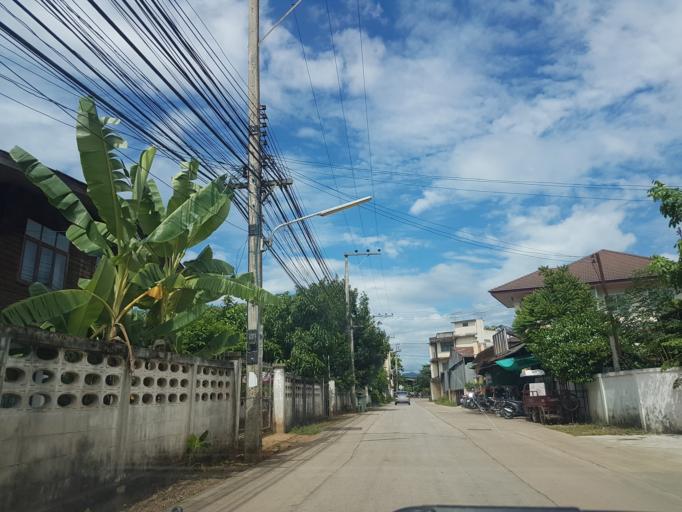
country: TH
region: Lampang
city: Ko Kha
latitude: 18.2399
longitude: 99.4398
